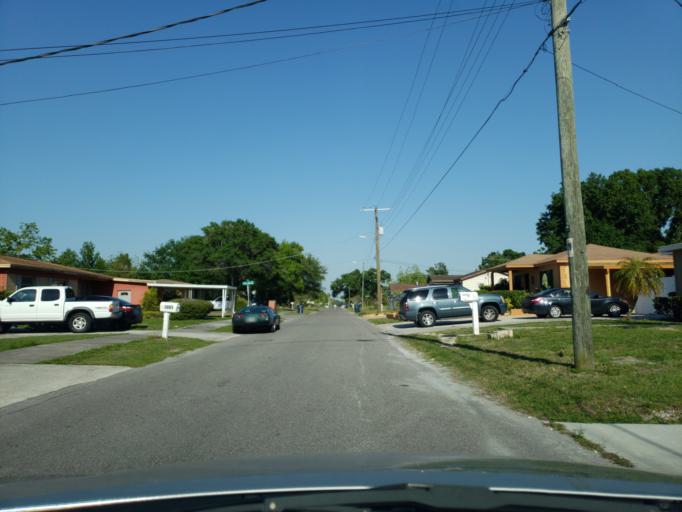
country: US
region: Florida
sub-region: Hillsborough County
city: Tampa
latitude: 27.9631
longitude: -82.4924
